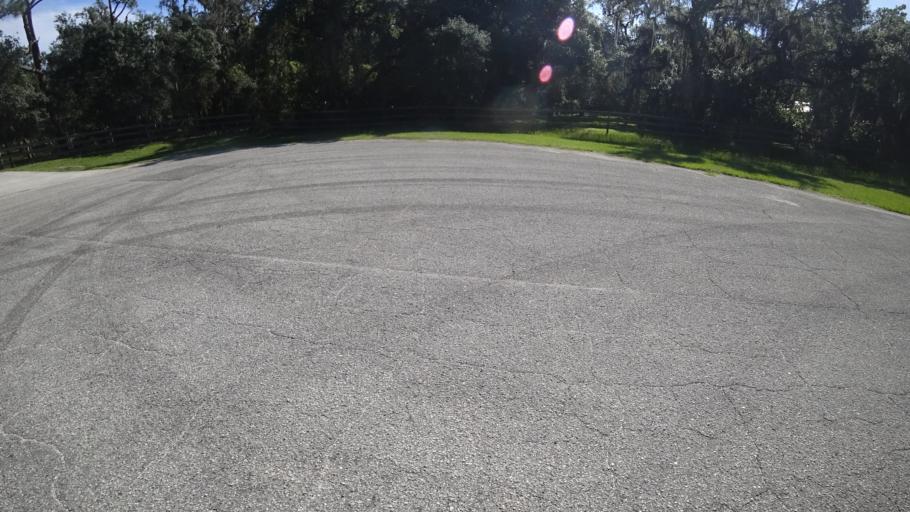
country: US
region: Florida
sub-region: Sarasota County
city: Lake Sarasota
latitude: 27.2771
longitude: -82.2294
